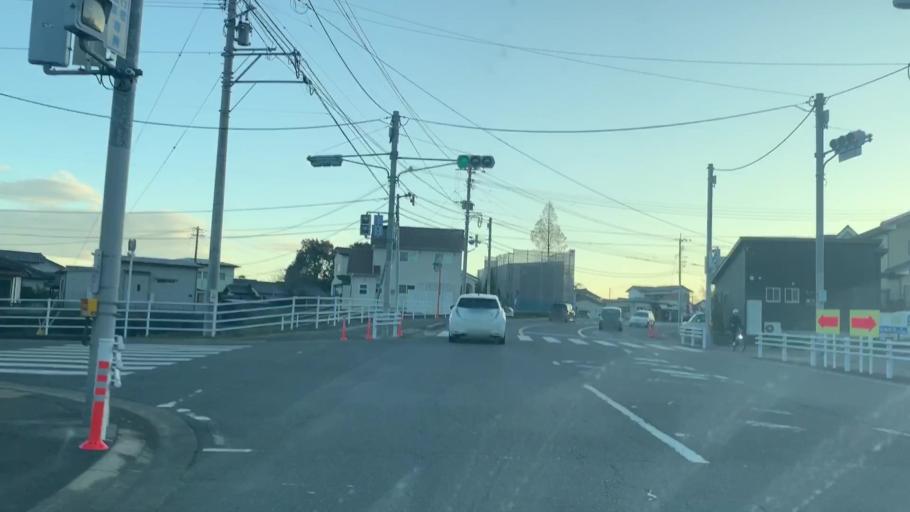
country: JP
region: Saga Prefecture
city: Takeocho-takeo
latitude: 33.2073
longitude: 130.0268
